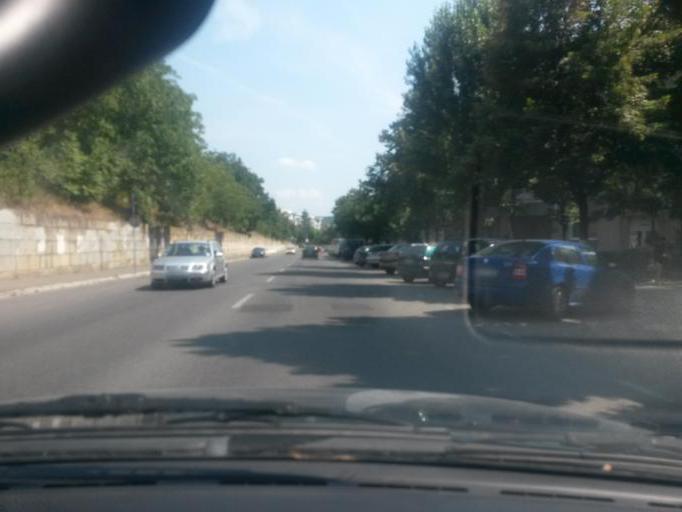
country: RO
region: Mures
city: Targu-Mures
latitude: 46.5402
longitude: 24.5826
